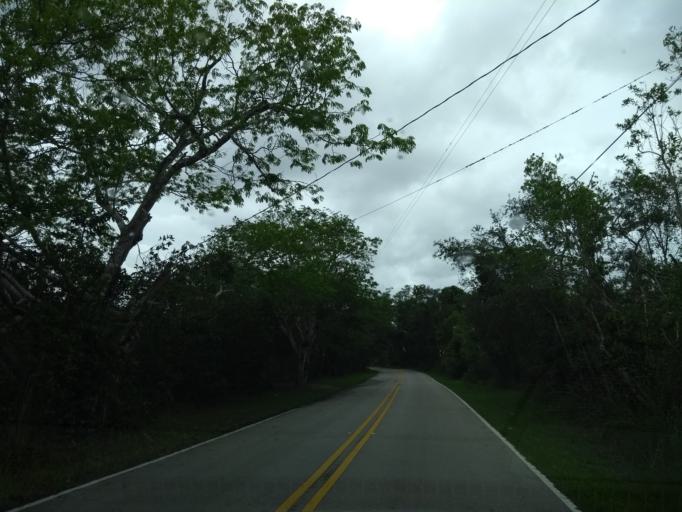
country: US
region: Florida
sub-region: Miami-Dade County
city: The Hammocks
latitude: 25.7612
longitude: -80.9208
